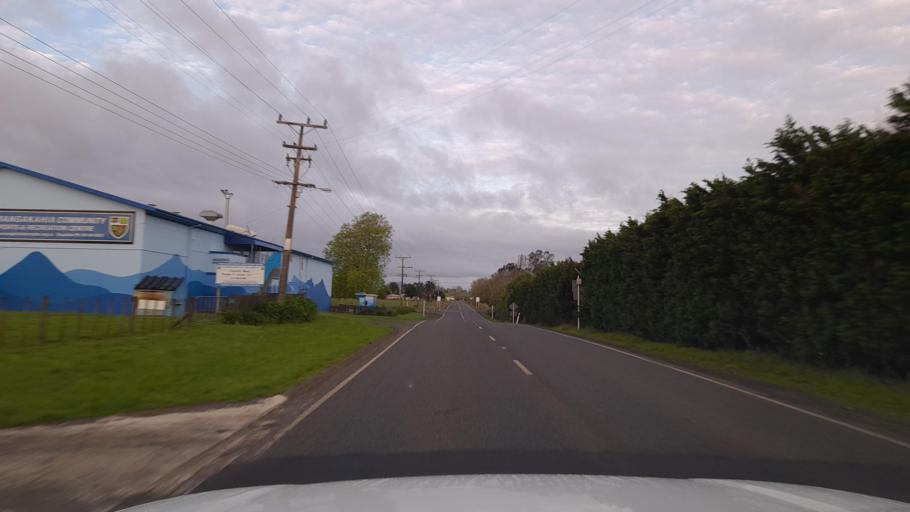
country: NZ
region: Northland
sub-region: Whangarei
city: Maungatapere
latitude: -35.7378
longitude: 174.1373
